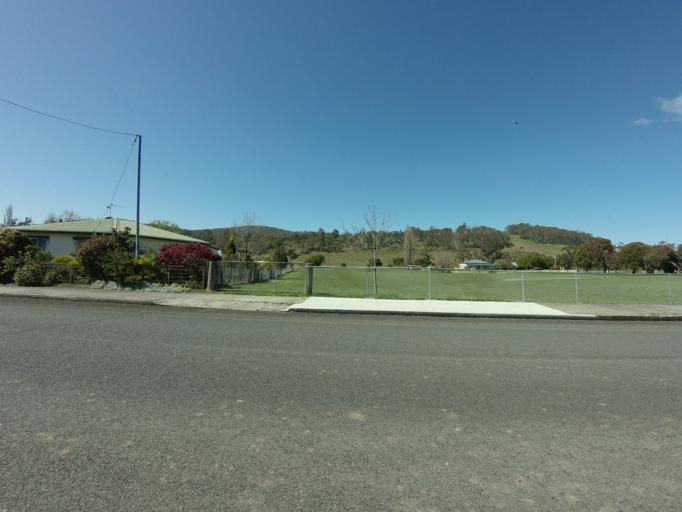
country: AU
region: Tasmania
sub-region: Derwent Valley
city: New Norfolk
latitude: -42.6177
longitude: 146.7161
